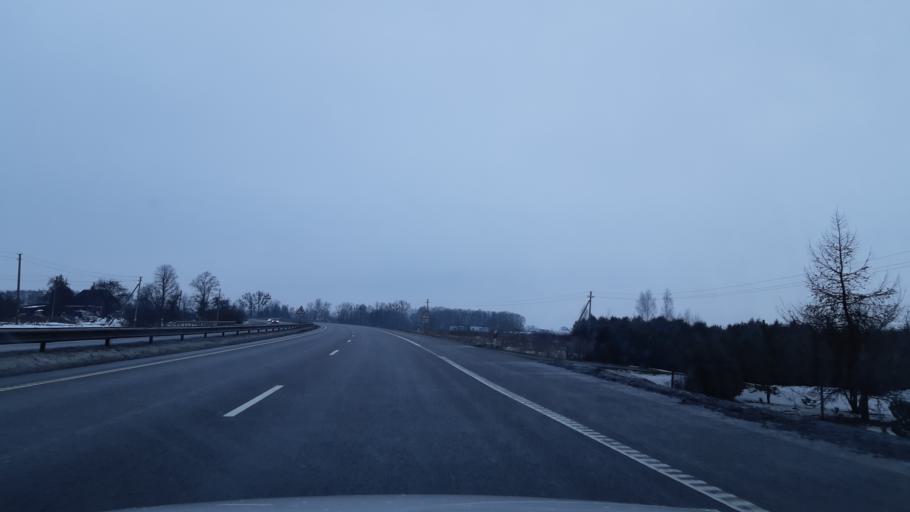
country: LT
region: Kauno apskritis
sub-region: Kauno rajonas
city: Akademija (Kaunas)
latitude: 54.8874
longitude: 23.8193
